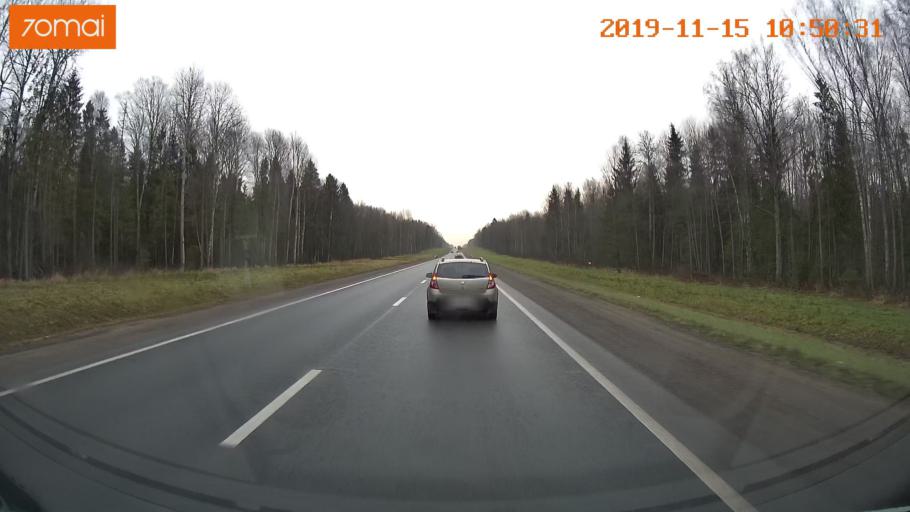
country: RU
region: Vologda
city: Chebsara
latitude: 59.1849
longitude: 38.6834
